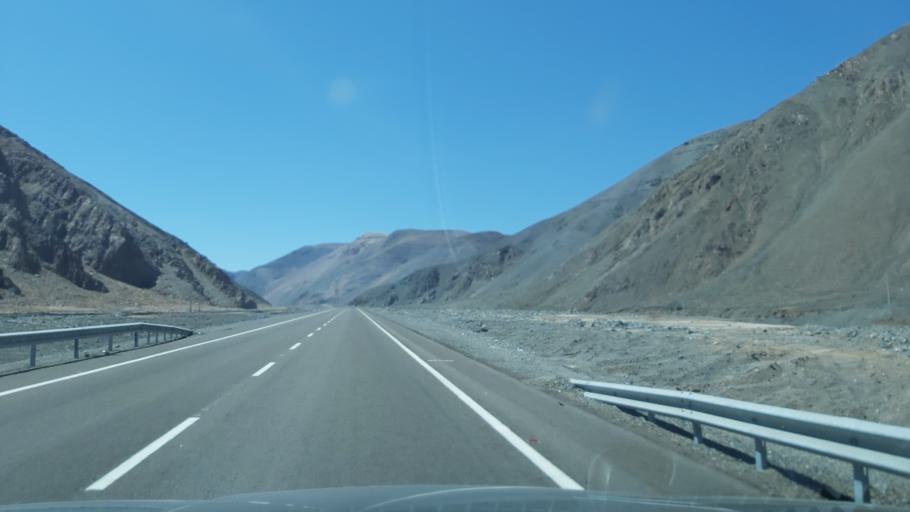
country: CL
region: Atacama
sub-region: Provincia de Chanaral
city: Diego de Almagro
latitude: -26.3503
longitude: -69.7380
